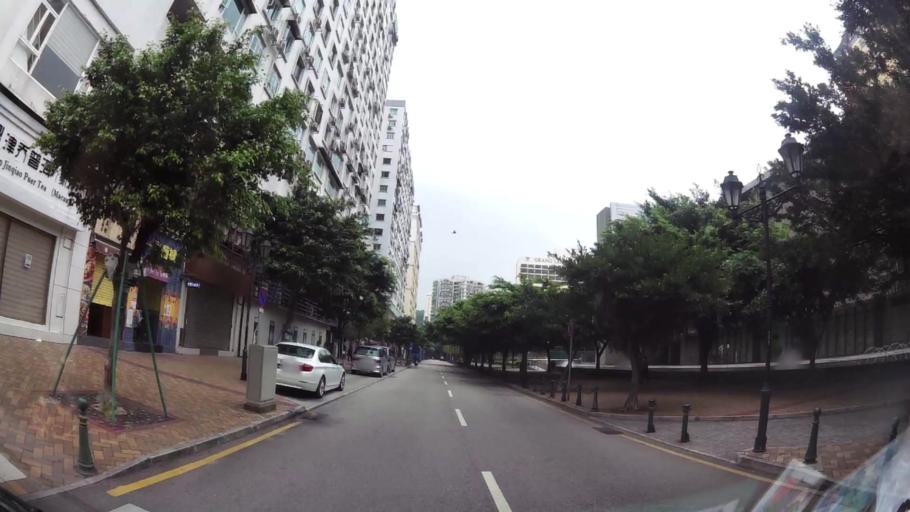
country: MO
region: Macau
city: Macau
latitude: 22.1899
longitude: 113.5538
